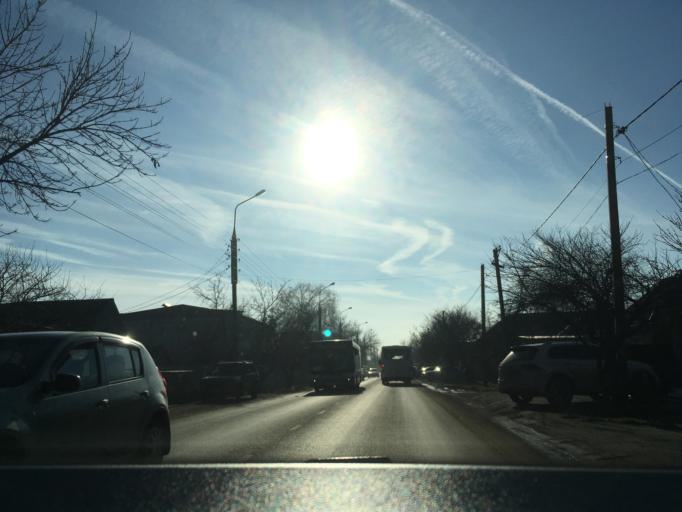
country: RU
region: Krasnodarskiy
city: Krasnodar
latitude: 45.1231
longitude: 39.0112
